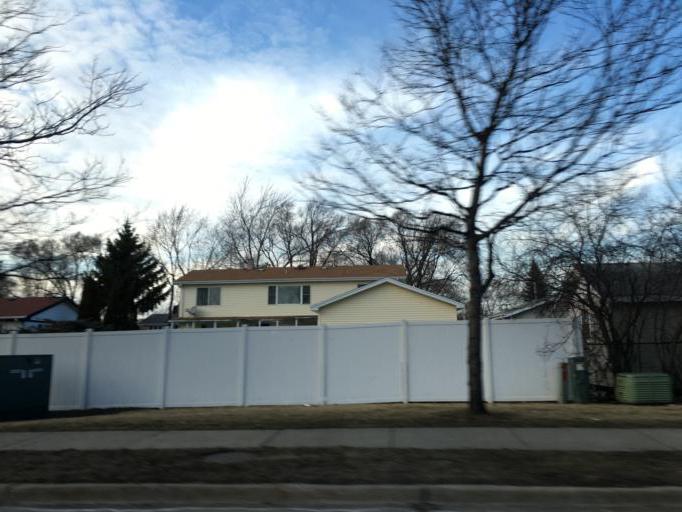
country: US
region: Illinois
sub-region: Cook County
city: Schaumburg
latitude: 42.0268
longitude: -88.0958
